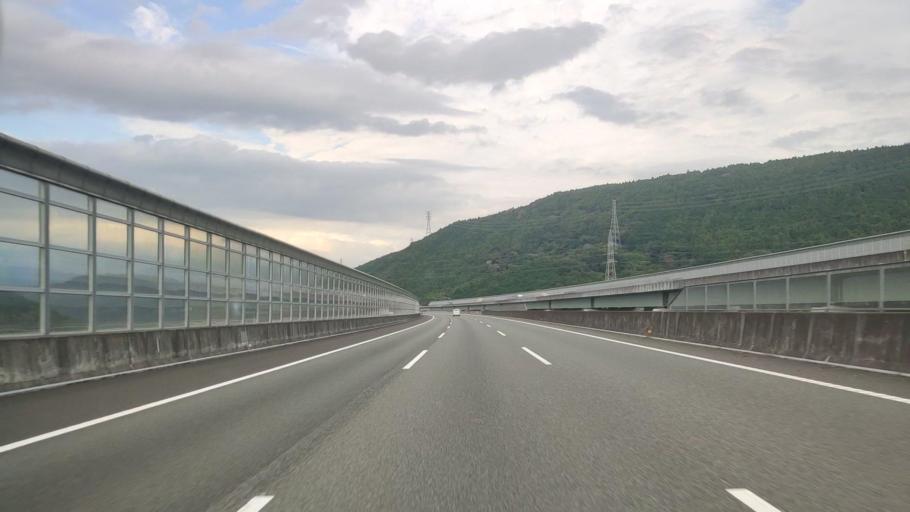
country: JP
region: Shizuoka
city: Fujinomiya
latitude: 35.1674
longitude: 138.5931
